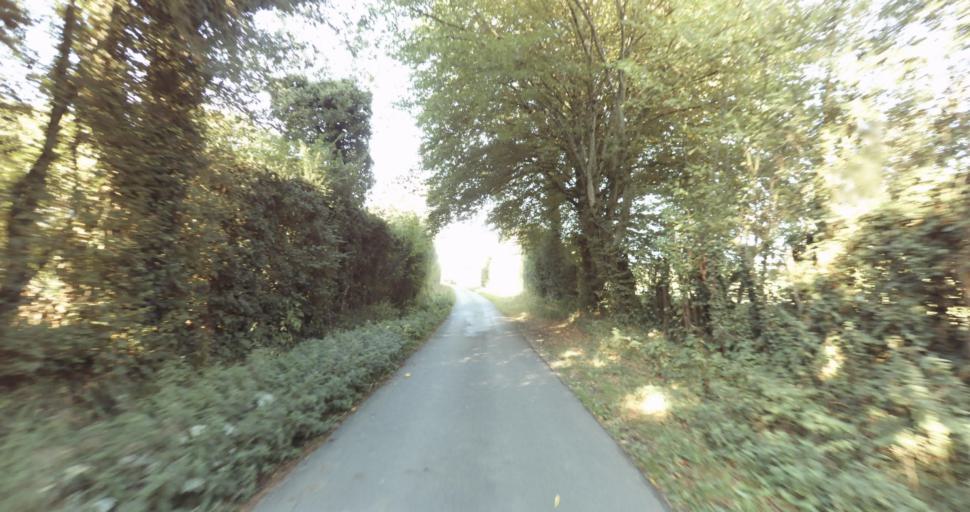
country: FR
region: Lower Normandy
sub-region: Departement de l'Orne
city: Vimoutiers
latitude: 48.8838
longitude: 0.1280
